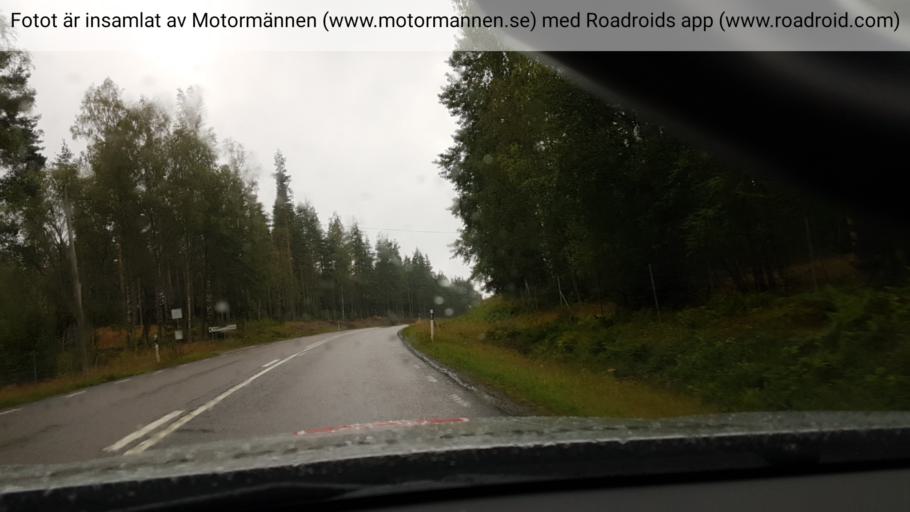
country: SE
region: Vaestra Goetaland
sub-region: Bengtsfors Kommun
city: Billingsfors
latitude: 59.0001
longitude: 12.2700
